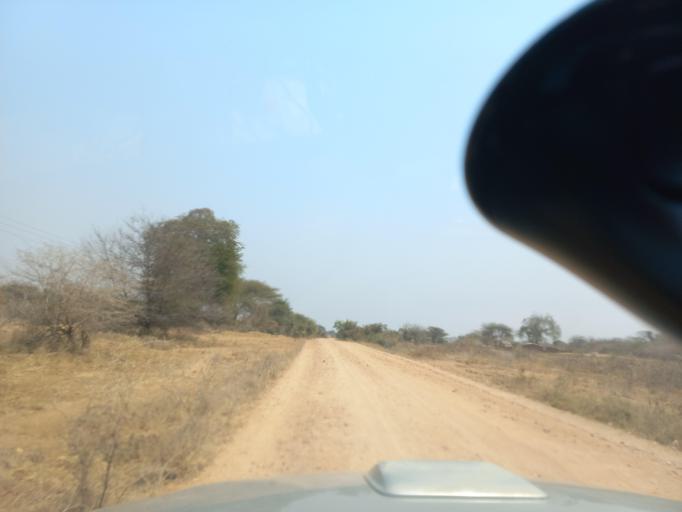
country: ZW
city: Chirundu
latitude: -15.9350
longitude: 28.8614
